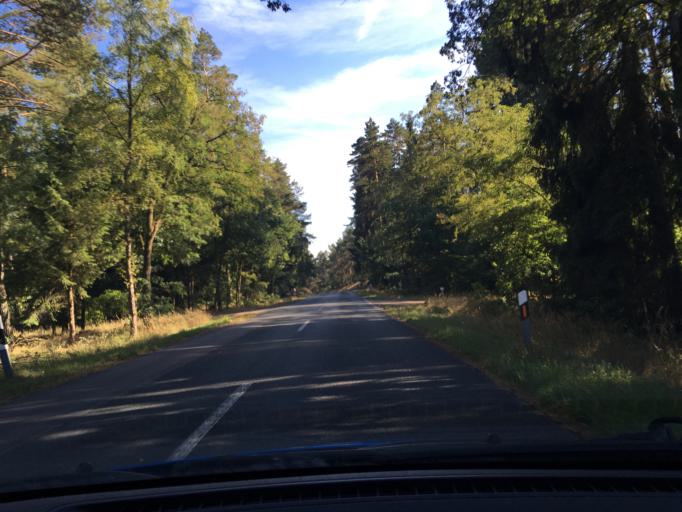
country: DE
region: Lower Saxony
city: Thomasburg
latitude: 53.2382
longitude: 10.7045
